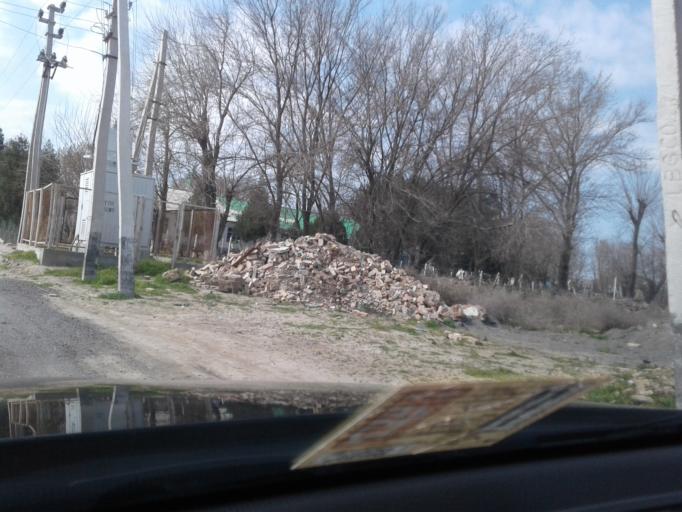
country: TM
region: Ahal
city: Abadan
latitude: 38.1211
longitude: 58.3503
